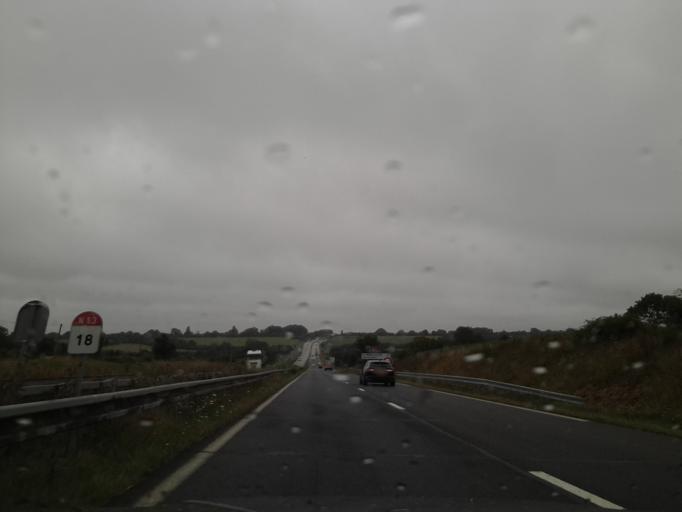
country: FR
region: Lower Normandy
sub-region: Departement de la Manche
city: Sainte-Mere-Eglise
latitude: 49.3850
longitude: -1.2994
